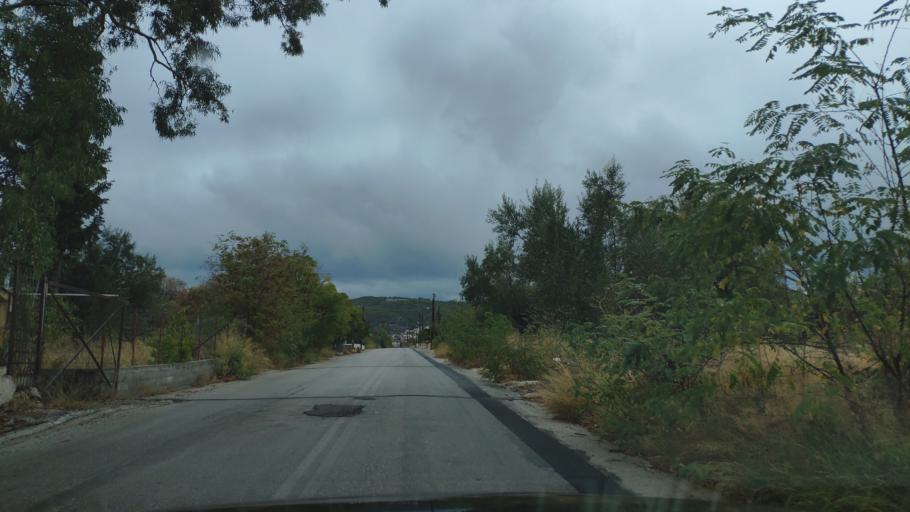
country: GR
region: Peloponnese
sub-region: Nomos Korinthias
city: Perachora
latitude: 38.0150
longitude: 22.9468
